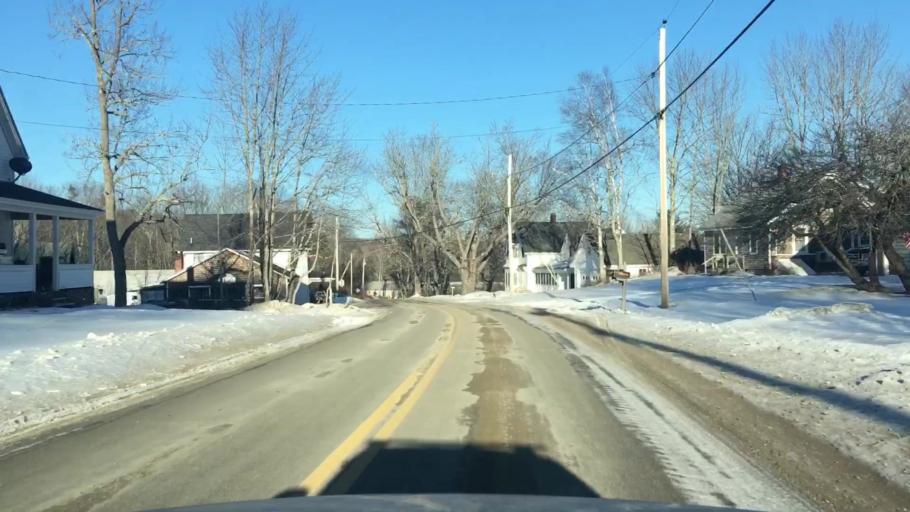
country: US
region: Maine
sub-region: Hancock County
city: Penobscot
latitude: 44.3965
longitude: -68.7082
